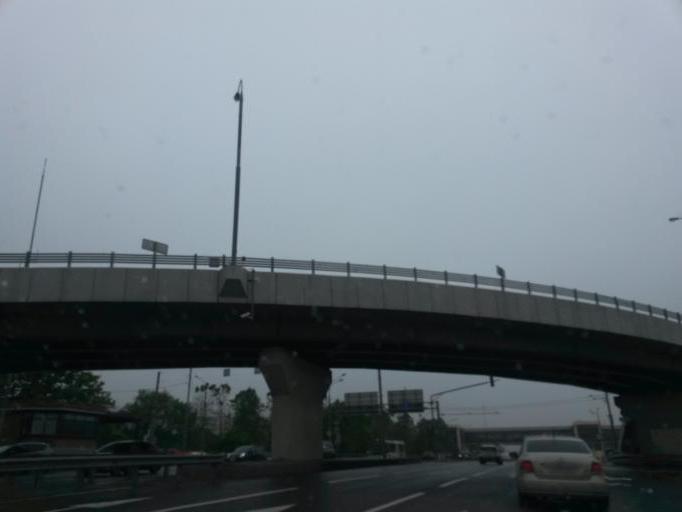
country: RU
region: Moscow
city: Tyoply Stan
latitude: 55.6120
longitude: 37.4938
